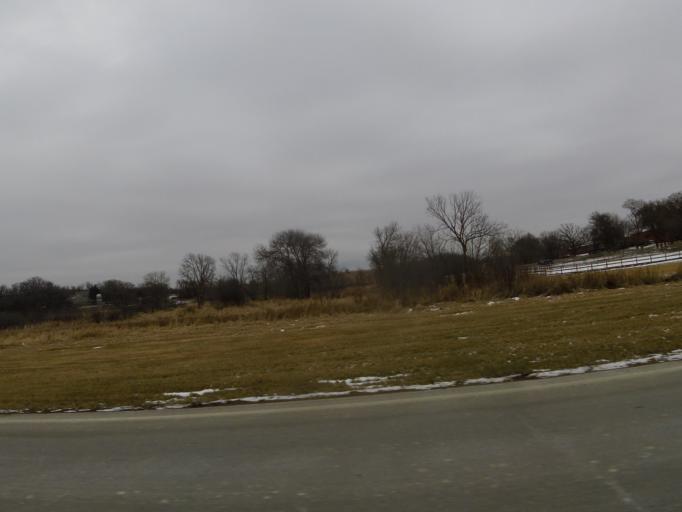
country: US
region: Minnesota
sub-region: Hennepin County
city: Medina
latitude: 45.0193
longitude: -93.6146
